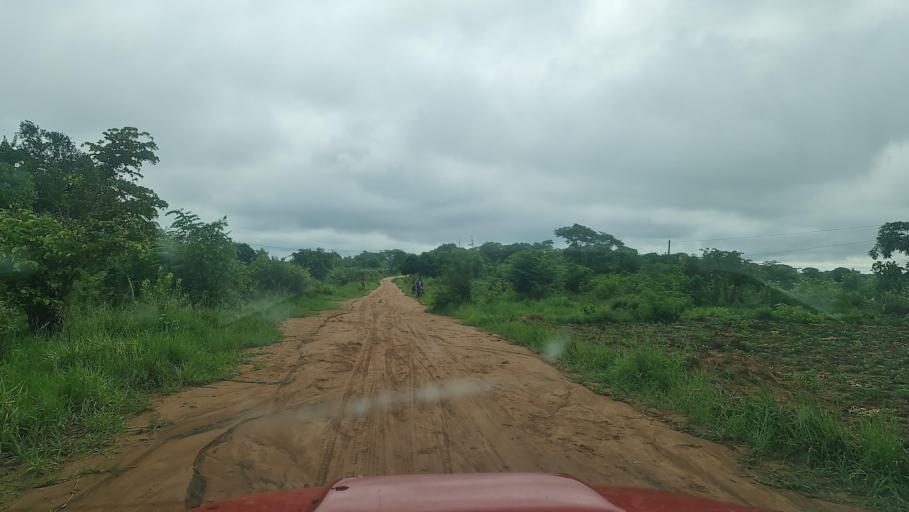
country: MW
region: Southern Region
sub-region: Nsanje District
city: Nsanje
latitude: -17.1931
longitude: 35.8499
